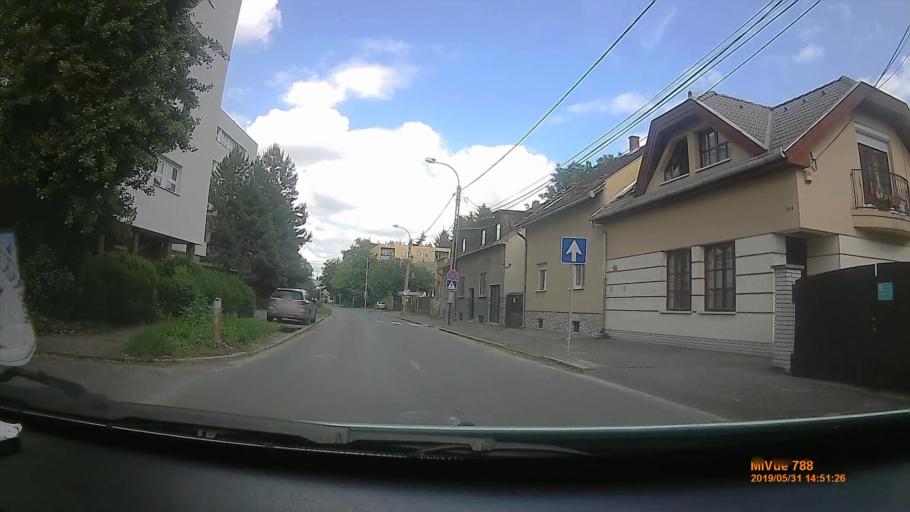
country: HU
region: Borsod-Abauj-Zemplen
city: Miskolc
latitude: 48.1015
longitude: 20.7731
